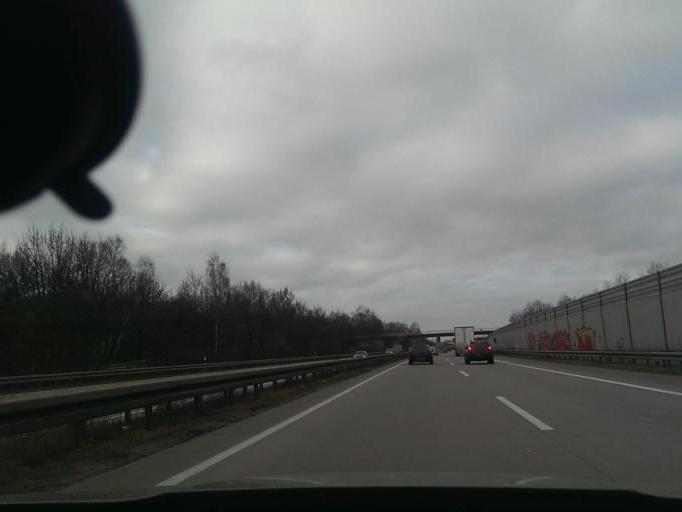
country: DE
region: Lower Saxony
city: Langenhagen
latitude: 52.4807
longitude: 9.7204
